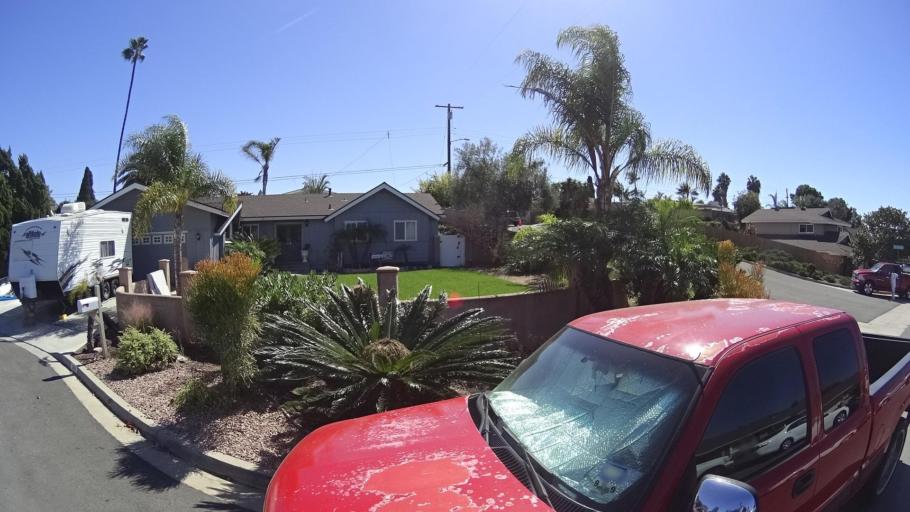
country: US
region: California
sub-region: San Diego County
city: Chula Vista
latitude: 32.6571
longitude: -117.0615
